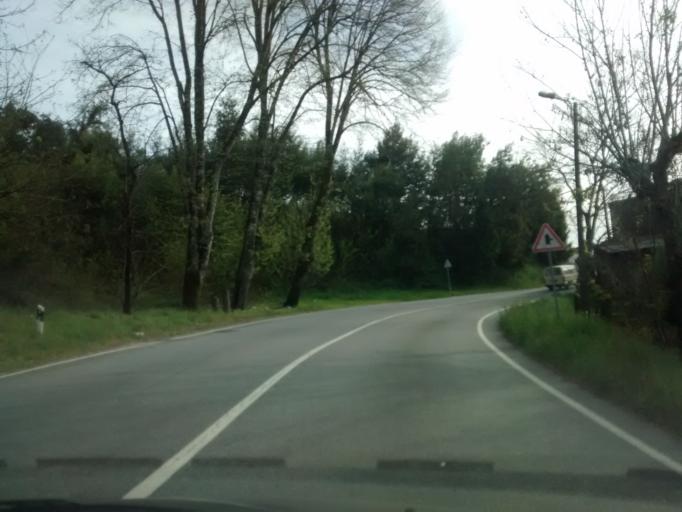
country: PT
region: Braga
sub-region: Braga
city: Braga
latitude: 41.5057
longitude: -8.4165
